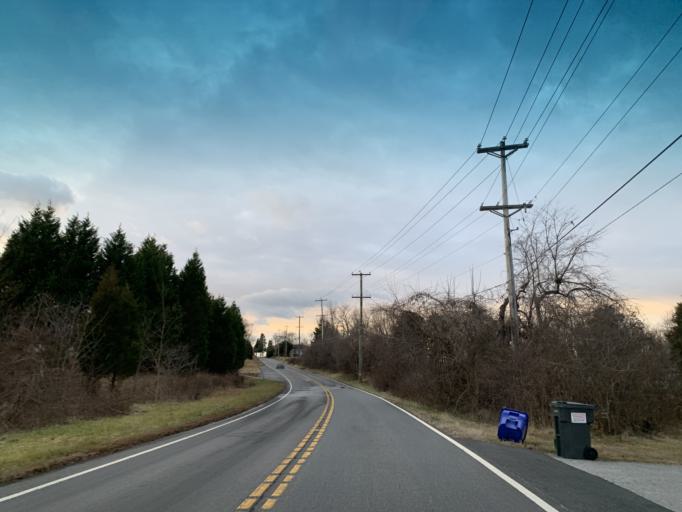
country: US
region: Maryland
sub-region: Harford County
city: South Bel Air
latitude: 39.6486
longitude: -76.2867
